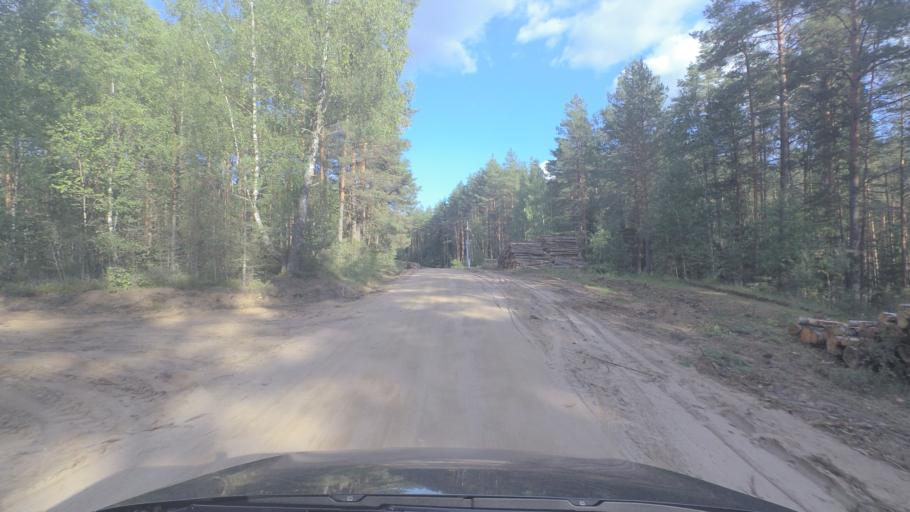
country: LT
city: Pabrade
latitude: 55.1539
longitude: 25.7803
